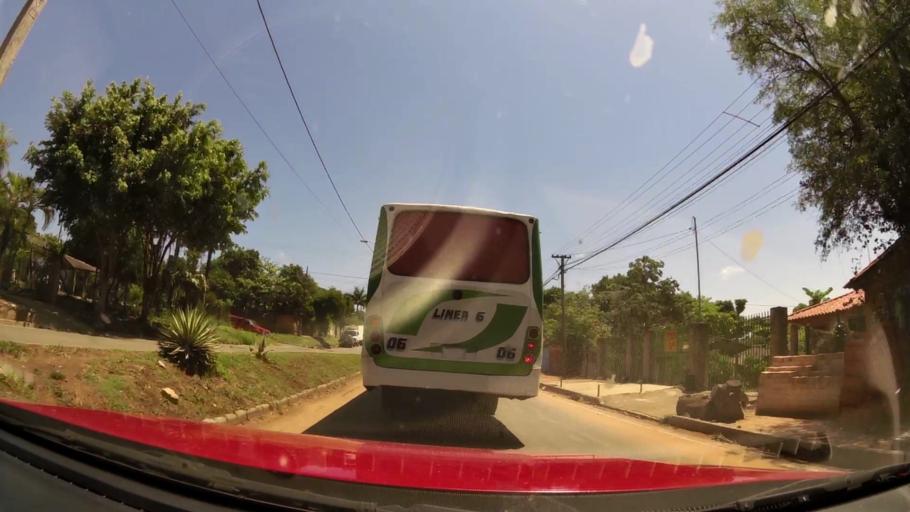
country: PY
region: Central
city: Colonia Mariano Roque Alonso
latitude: -25.2294
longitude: -57.5608
